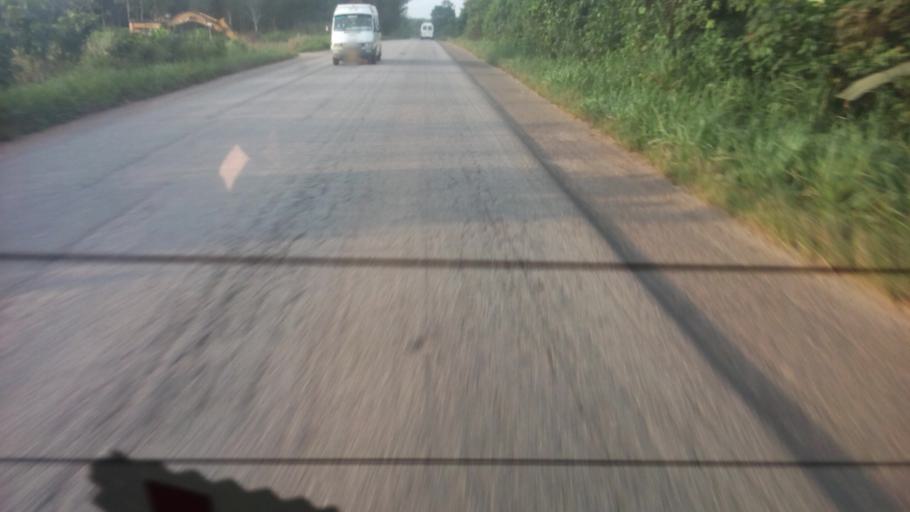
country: GH
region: Western
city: Tarkwa
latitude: 5.1968
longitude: -2.0314
